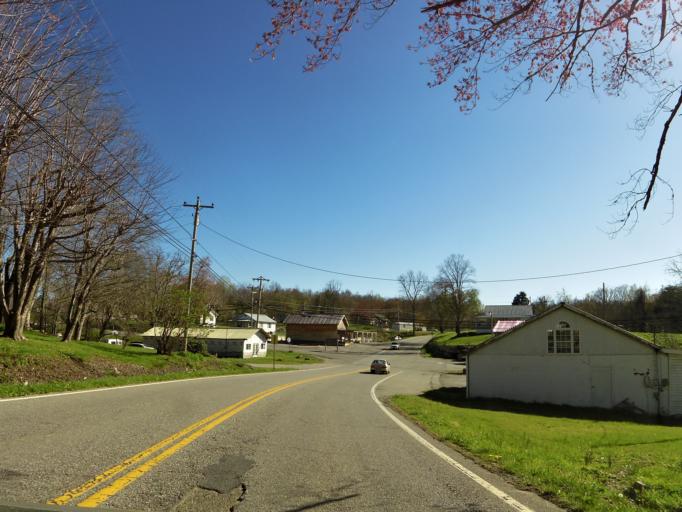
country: US
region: Tennessee
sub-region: Scott County
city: Huntsville
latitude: 36.4060
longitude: -84.4357
